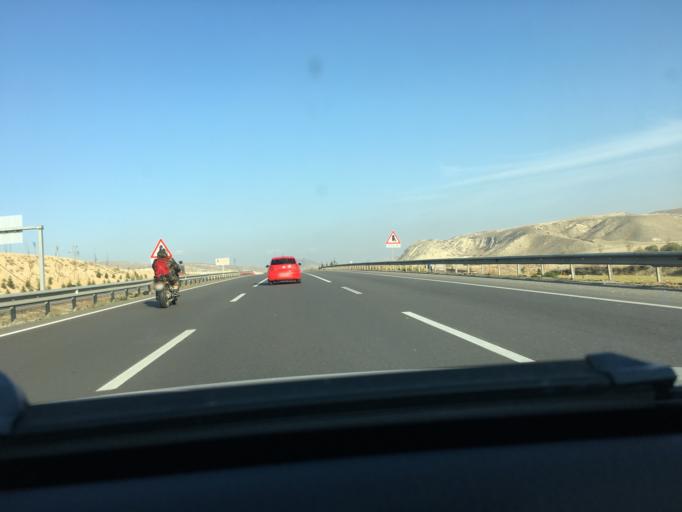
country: TR
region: Ankara
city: Temelli
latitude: 39.7572
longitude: 32.4521
